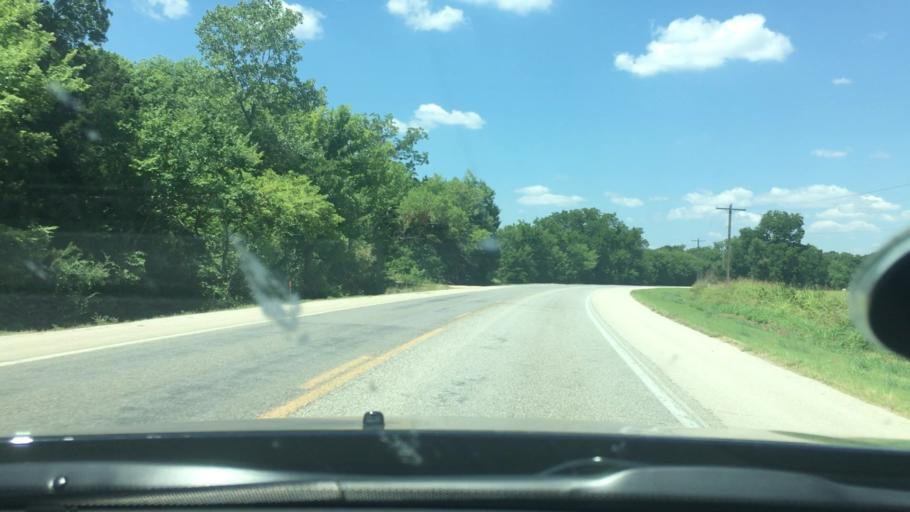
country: US
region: Oklahoma
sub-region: Marshall County
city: Oakland
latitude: 34.1735
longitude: -96.8519
